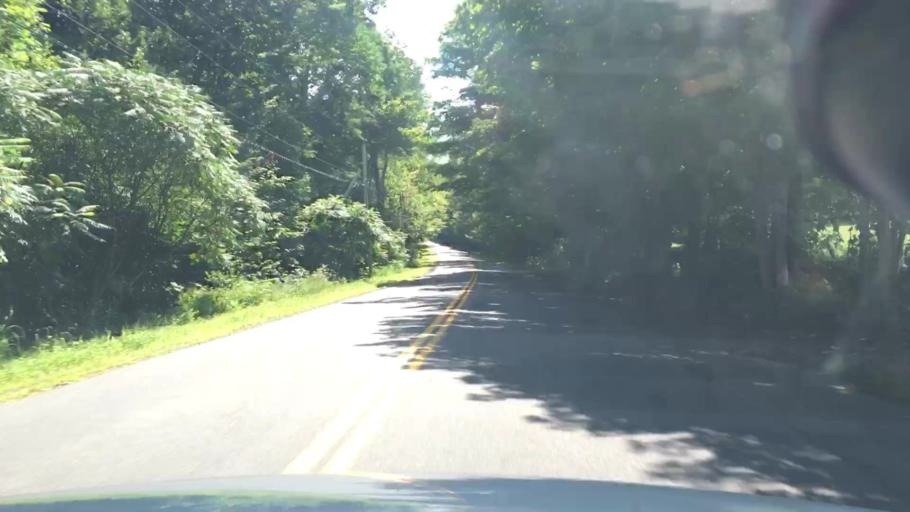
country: US
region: Maine
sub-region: Somerset County
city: Skowhegan
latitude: 44.7318
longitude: -69.7092
